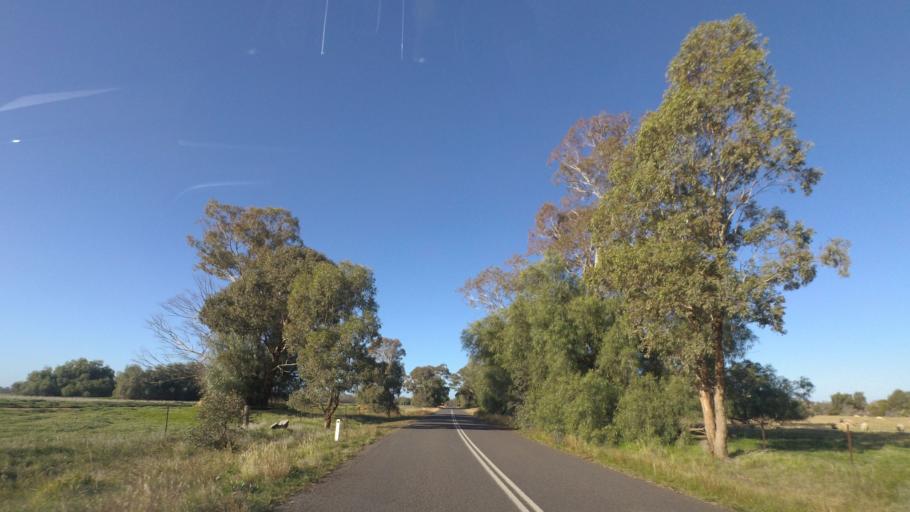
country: AU
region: Victoria
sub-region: Greater Bendigo
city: Epsom
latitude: -36.6466
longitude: 144.5334
